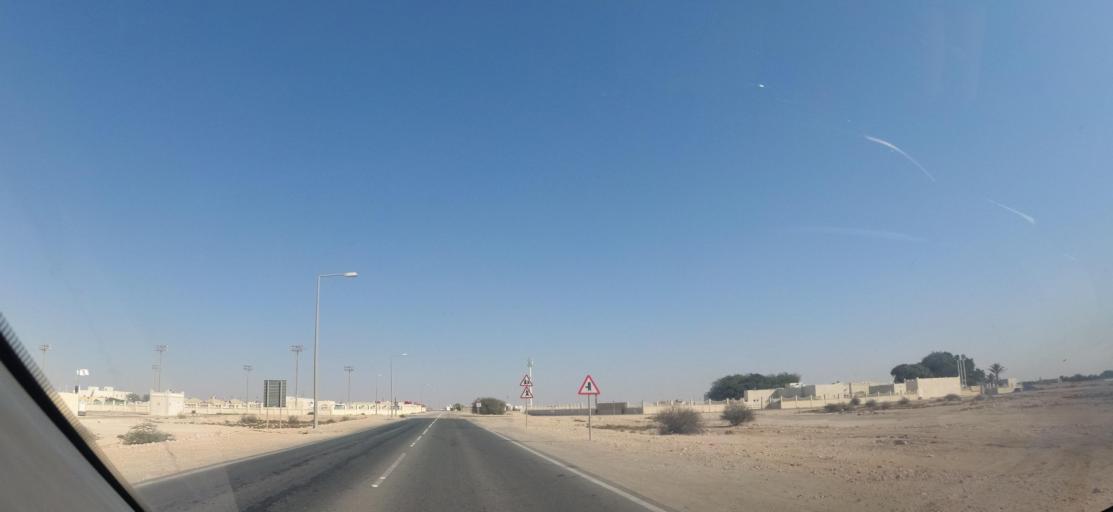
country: QA
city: Al Jumayliyah
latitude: 25.6182
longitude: 51.0800
